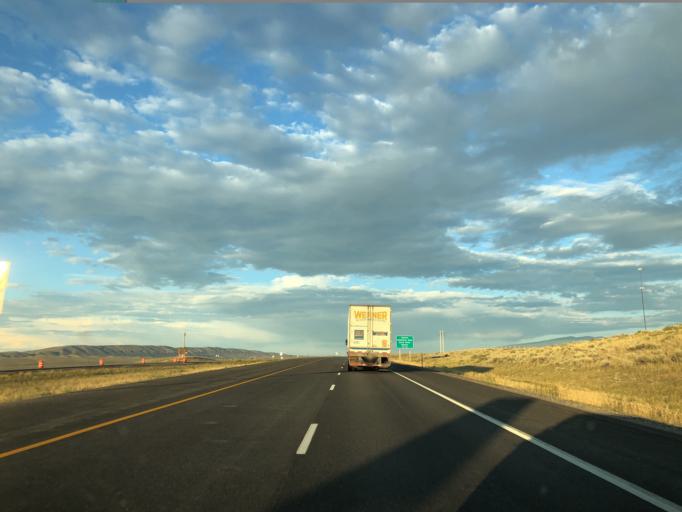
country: US
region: Wyoming
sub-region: Carbon County
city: Saratoga
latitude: 41.7419
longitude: -106.8520
